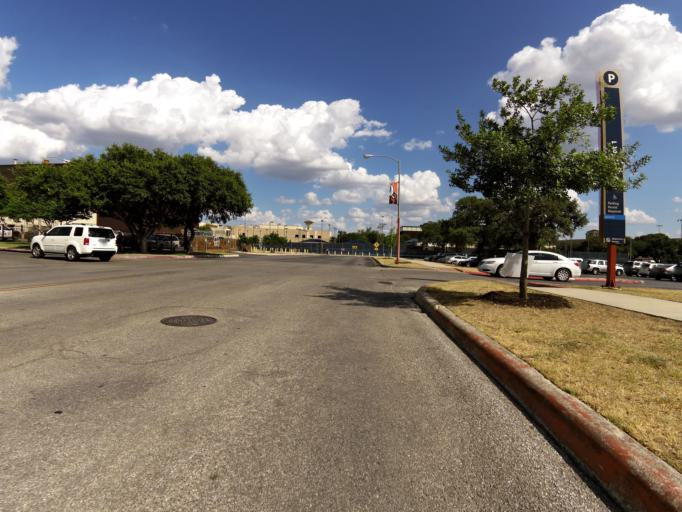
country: US
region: Texas
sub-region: Bexar County
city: Helotes
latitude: 29.5849
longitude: -98.6222
